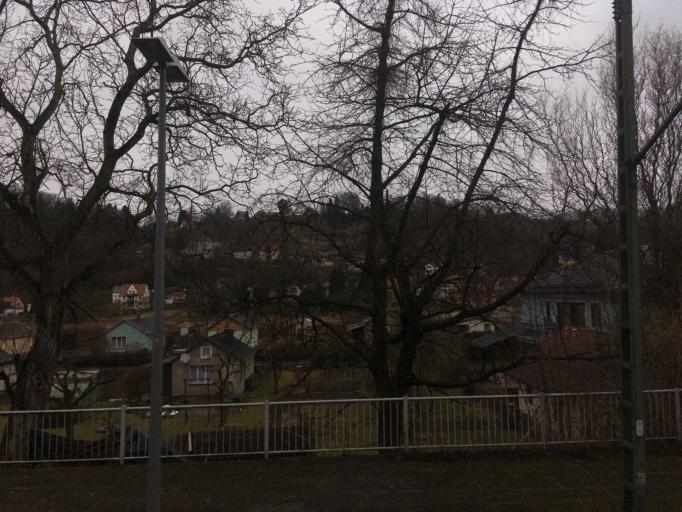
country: DE
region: Saxony
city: Stadt Wehlen
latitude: 50.9535
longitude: 14.0311
